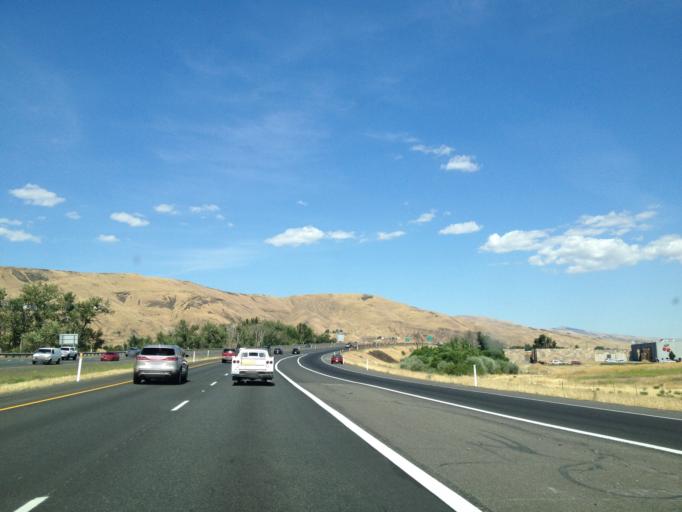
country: US
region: Washington
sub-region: Yakima County
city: Selah
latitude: 46.6252
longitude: -120.5273
